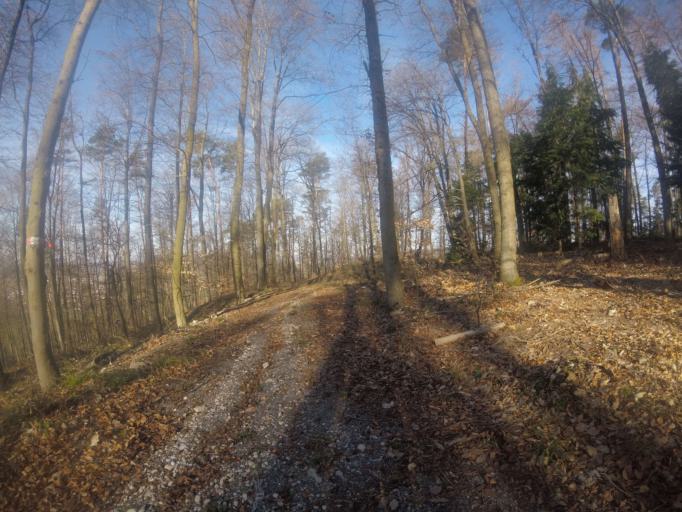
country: DE
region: Baden-Wuerttemberg
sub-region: Regierungsbezirk Stuttgart
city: Oberstenfeld
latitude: 49.0464
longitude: 9.3457
